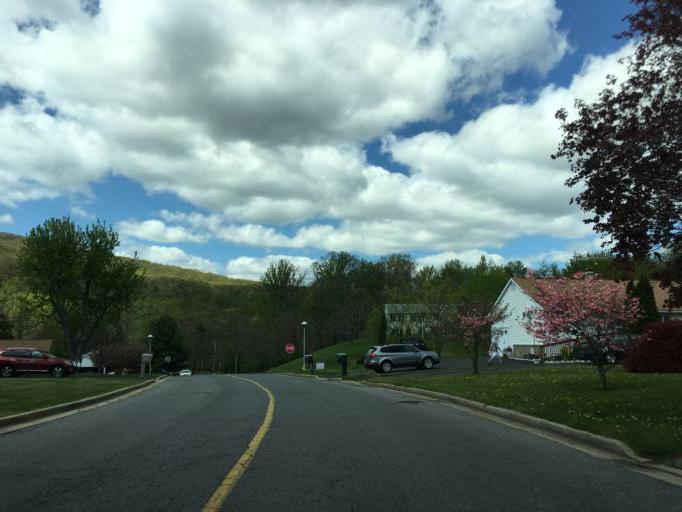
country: US
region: Maryland
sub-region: Frederick County
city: Thurmont
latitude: 39.6197
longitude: -77.4212
